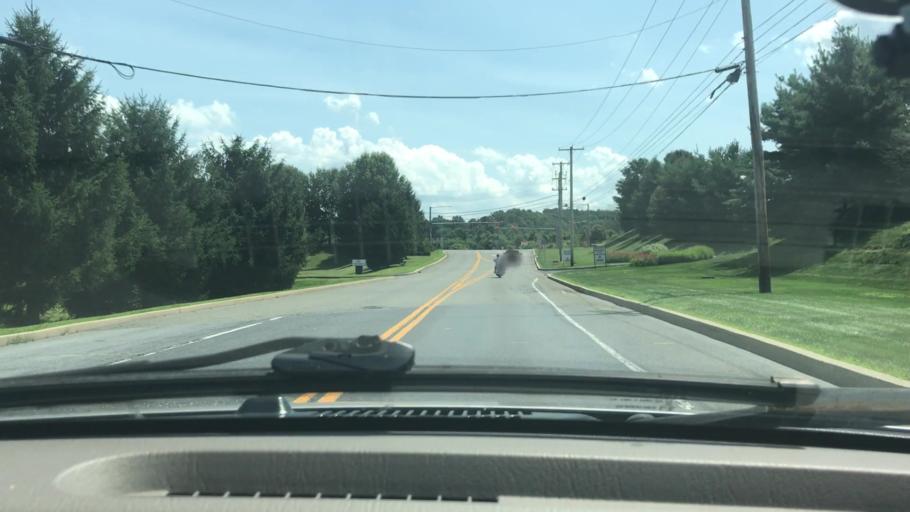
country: US
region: Pennsylvania
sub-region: Dauphin County
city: Middletown
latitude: 40.2318
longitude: -76.7378
